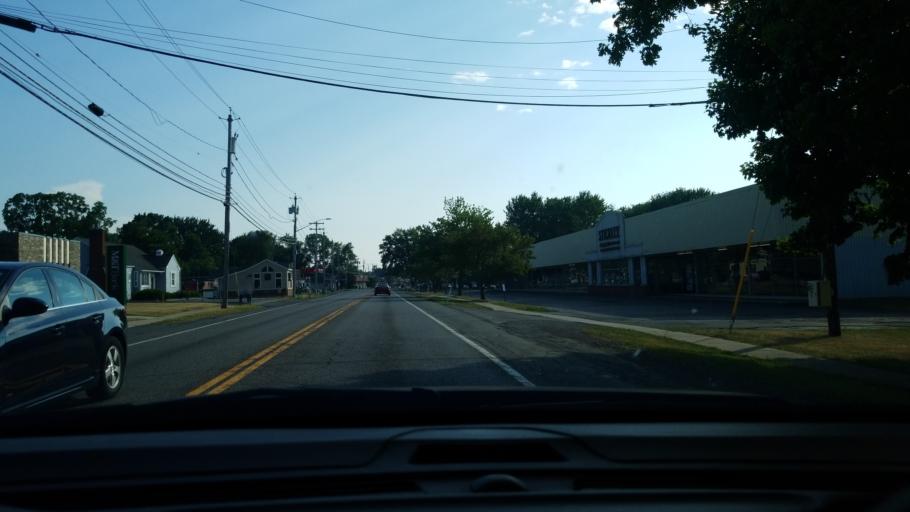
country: US
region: New York
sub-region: Onondaga County
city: North Syracuse
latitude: 43.1266
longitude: -76.1369
